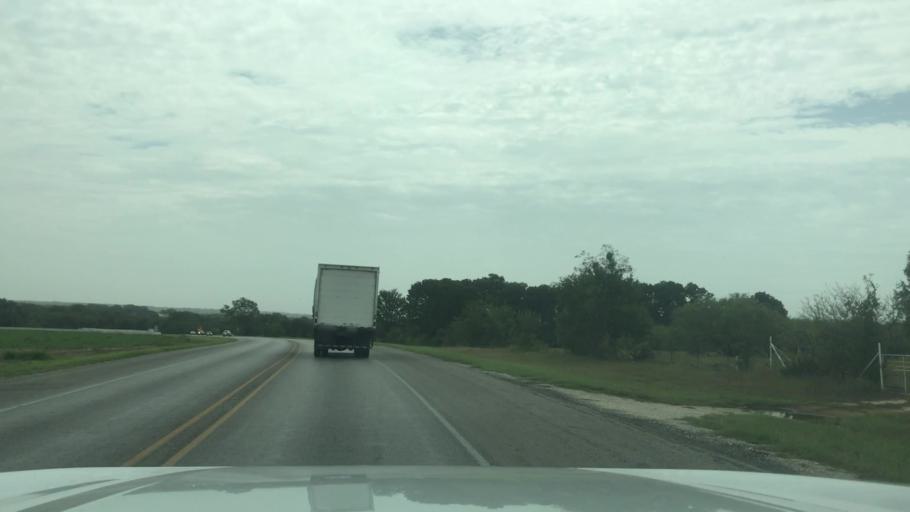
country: US
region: Texas
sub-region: Comanche County
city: De Leon
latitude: 32.1054
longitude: -98.4888
